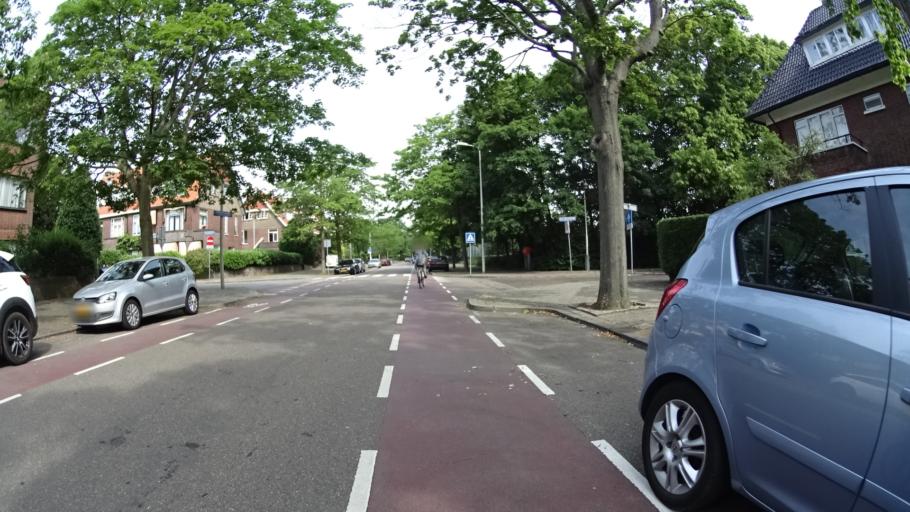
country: NL
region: South Holland
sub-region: Gemeente Den Haag
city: The Hague
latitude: 52.0946
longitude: 4.3231
